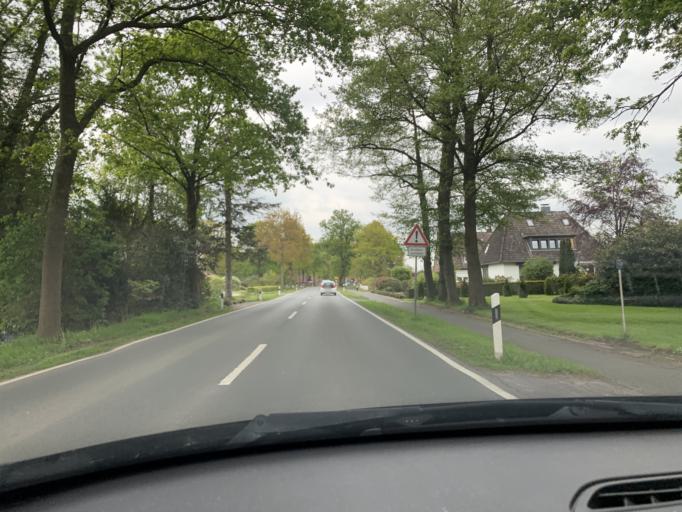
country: DE
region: Lower Saxony
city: Bad Zwischenahn
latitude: 53.2189
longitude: 8.0102
